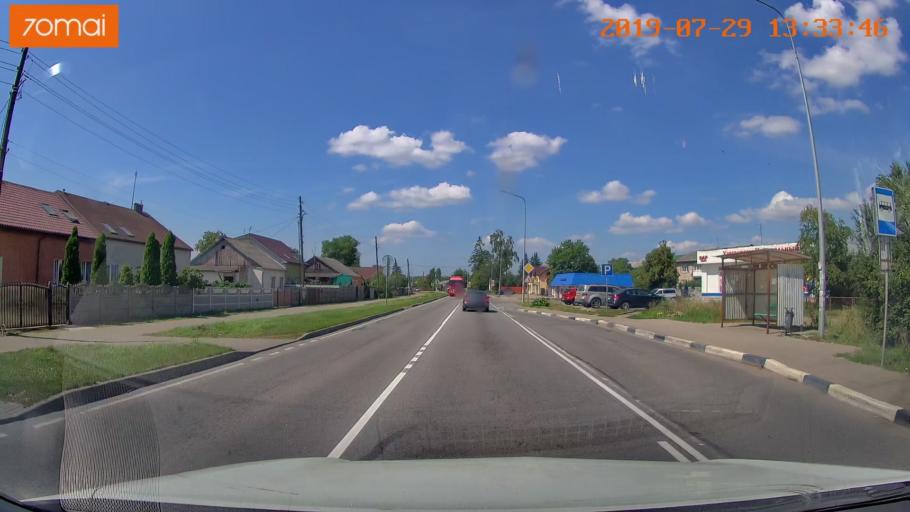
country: RU
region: Kaliningrad
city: Volochayevskoye
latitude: 54.6994
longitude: 20.2240
